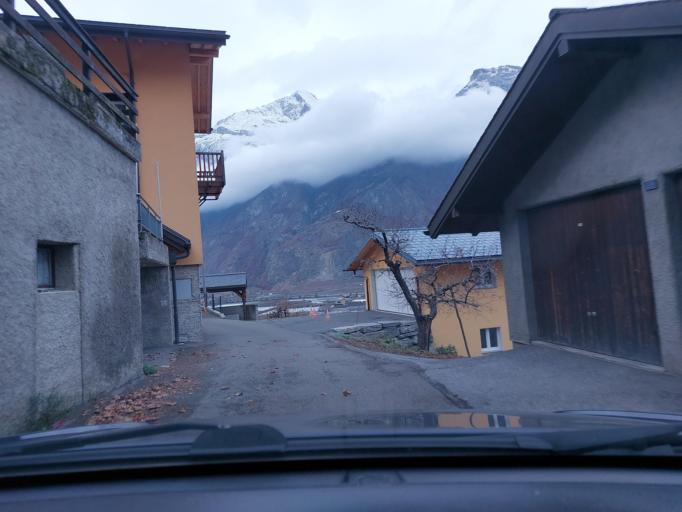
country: CH
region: Valais
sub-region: Martigny District
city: Saxon
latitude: 46.1455
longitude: 7.1778
